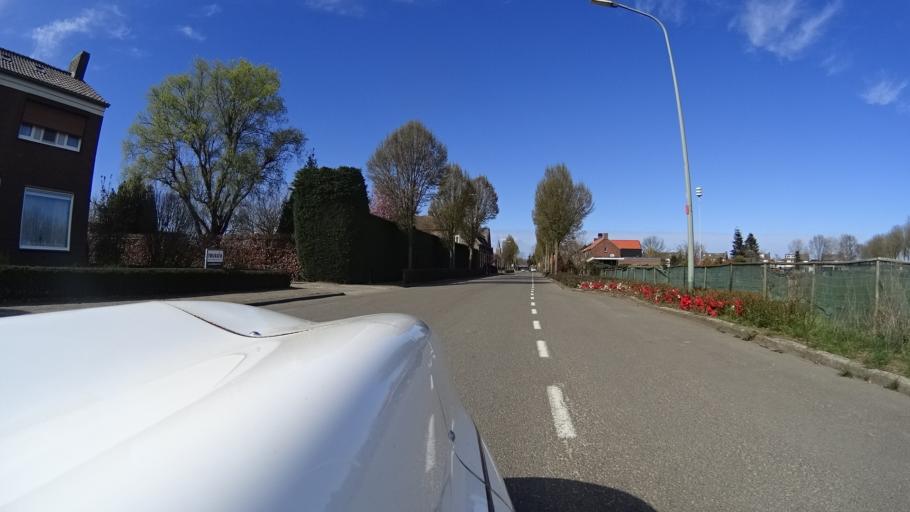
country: NL
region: Limburg
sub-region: Gemeente Venlo
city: Arcen
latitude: 51.4906
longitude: 6.1615
